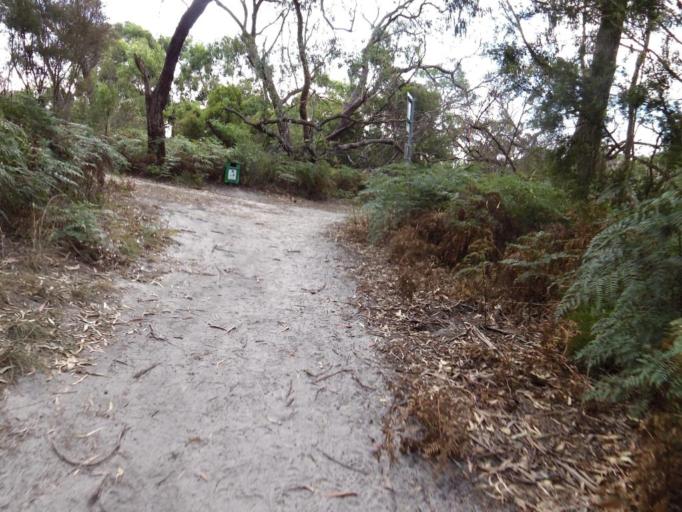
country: AU
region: Victoria
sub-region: Frankston
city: Frankston South
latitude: -38.1692
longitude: 145.1284
